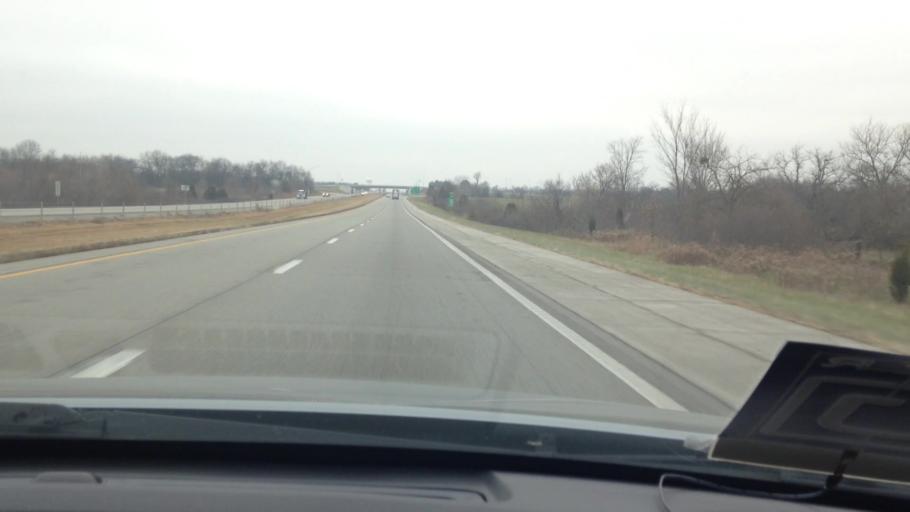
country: US
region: Missouri
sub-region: Cass County
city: Peculiar
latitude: 38.7332
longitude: -94.4644
